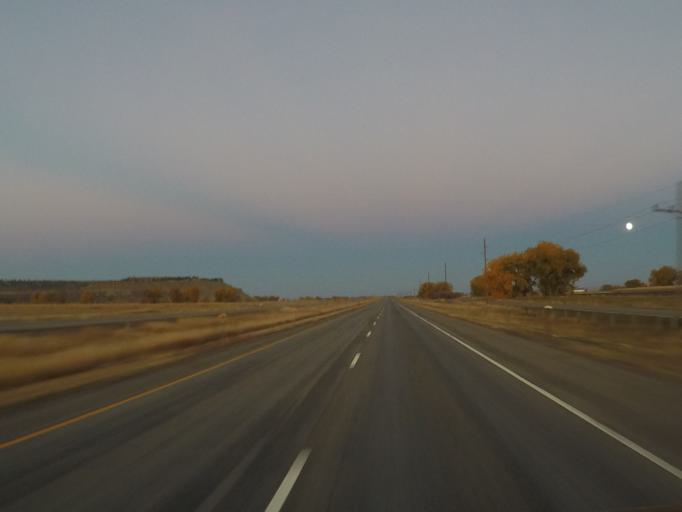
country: US
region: Montana
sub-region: Yellowstone County
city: Laurel
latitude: 45.6246
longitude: -108.9580
